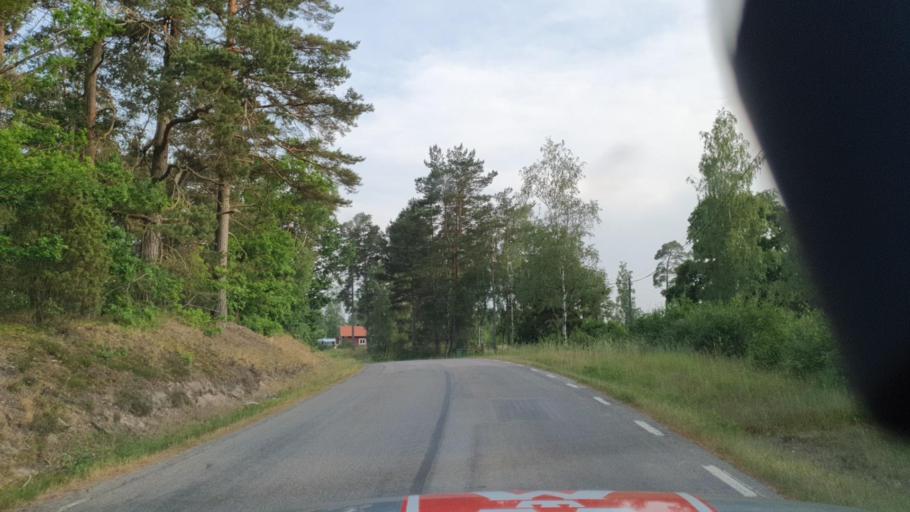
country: SE
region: Kalmar
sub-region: Torsas Kommun
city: Torsas
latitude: 56.4765
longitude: 16.0906
